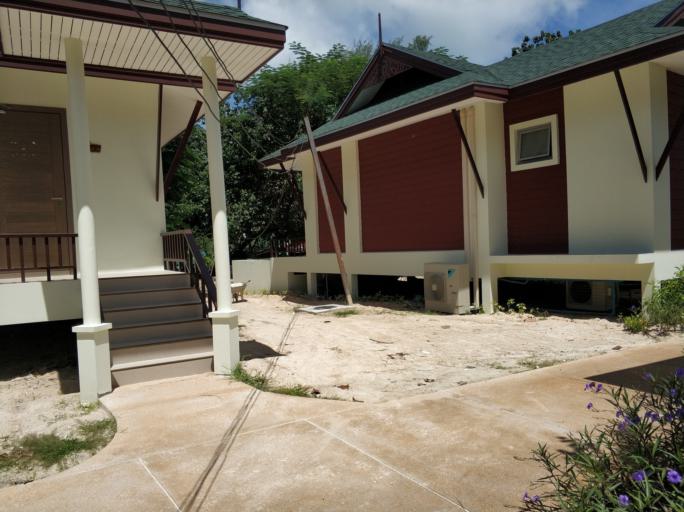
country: TH
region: Phangnga
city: Ban Phru Nai
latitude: 7.7404
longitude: 98.7719
